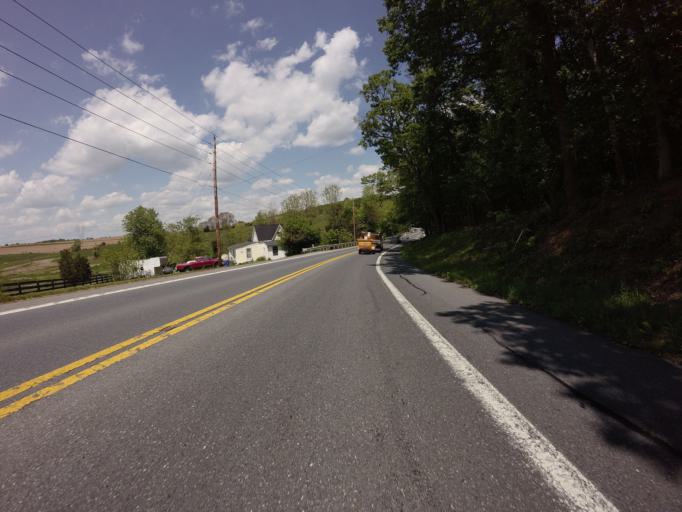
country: US
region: Maryland
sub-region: Frederick County
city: Green Valley
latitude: 39.3359
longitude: -77.2726
